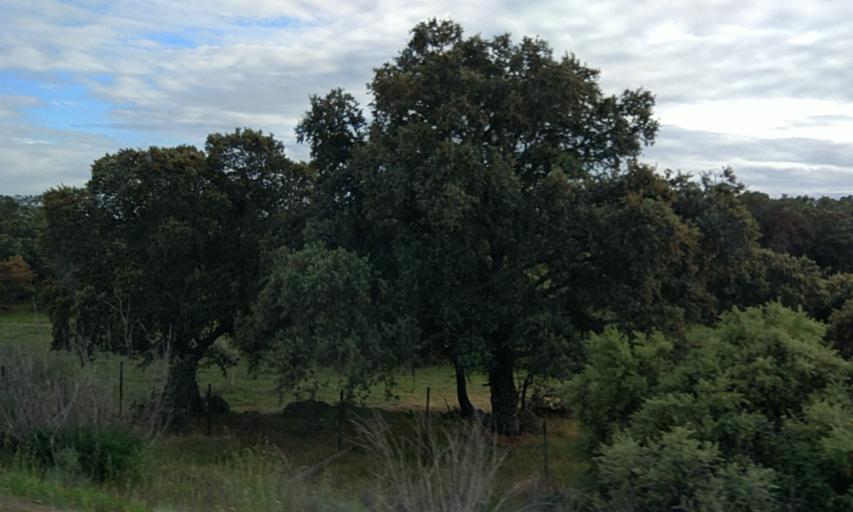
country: ES
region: Extremadura
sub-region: Provincia de Caceres
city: Torrejoncillo
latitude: 39.9086
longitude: -6.4795
